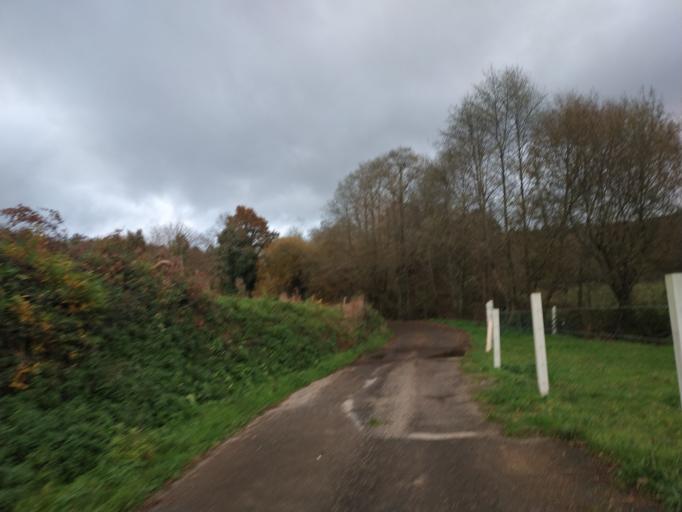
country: ES
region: Galicia
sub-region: Provincia de Pontevedra
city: Silleda
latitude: 42.7823
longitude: -8.1686
